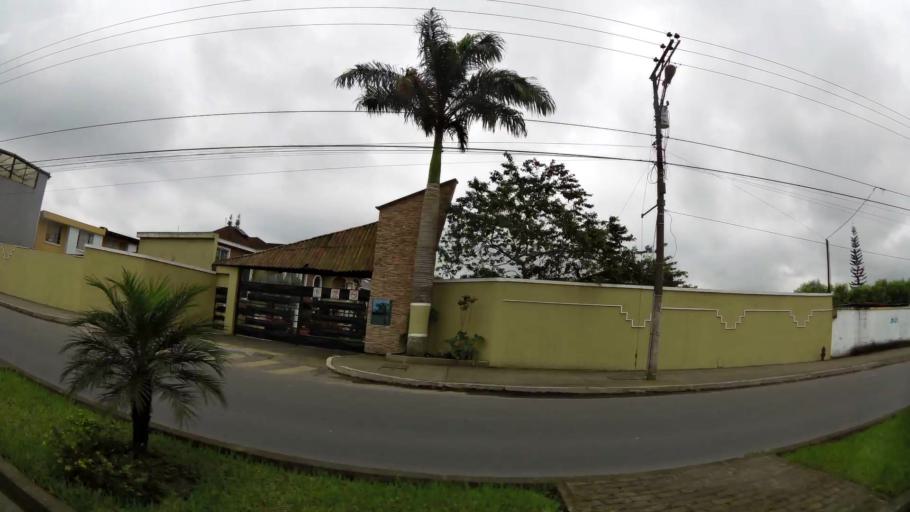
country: EC
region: Santo Domingo de los Tsachilas
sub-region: Canton Santo Domingo de los Colorados
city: Santo Domingo de los Colorados
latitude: -0.2600
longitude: -79.1398
